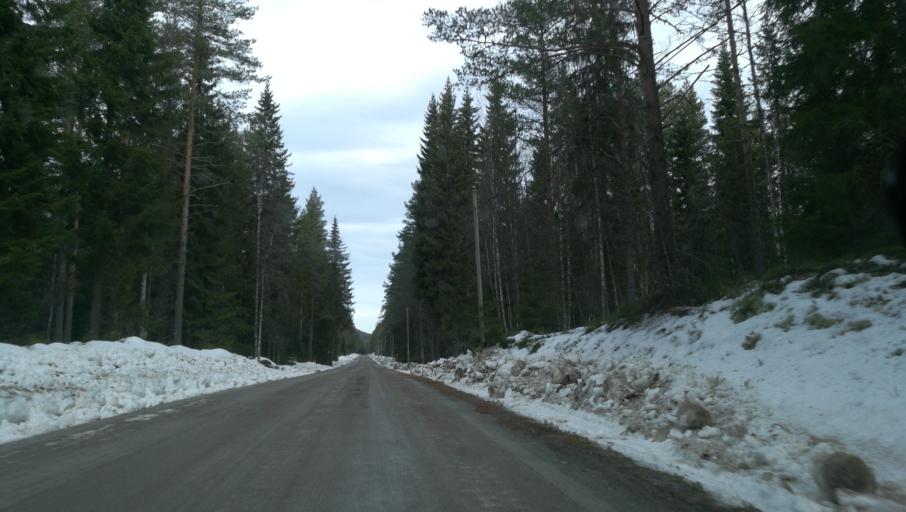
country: NO
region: Hedmark
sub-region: Grue
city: Kirkenaer
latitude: 60.4921
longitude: 12.5664
